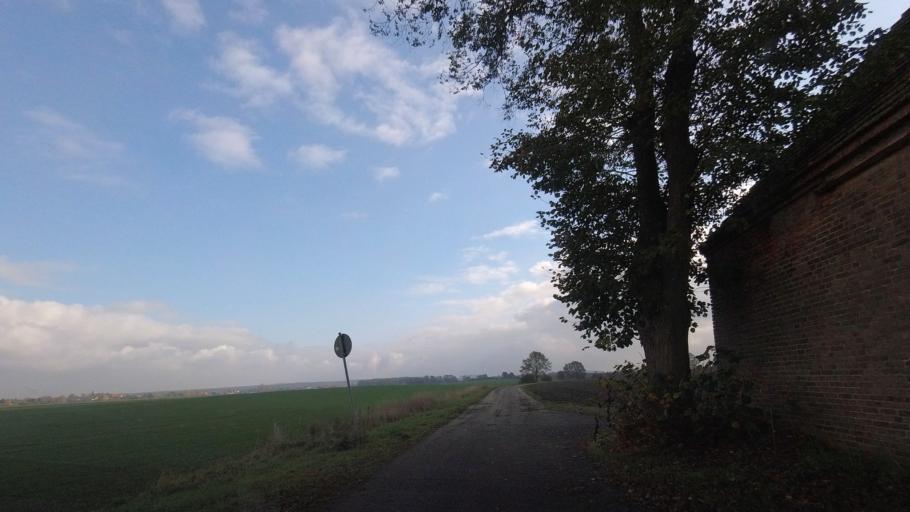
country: DE
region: Brandenburg
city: Juterbog
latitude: 51.9839
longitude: 13.0745
